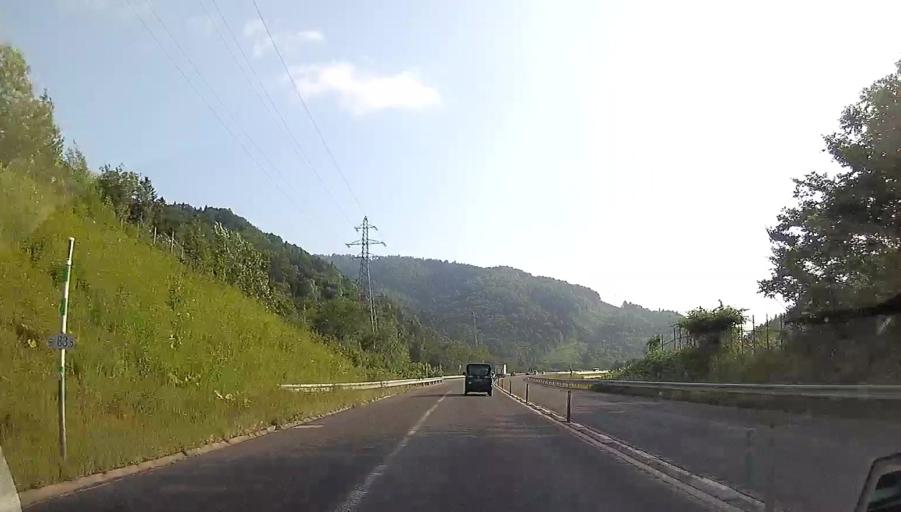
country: JP
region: Hokkaido
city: Shimo-furano
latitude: 43.0266
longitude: 142.4524
